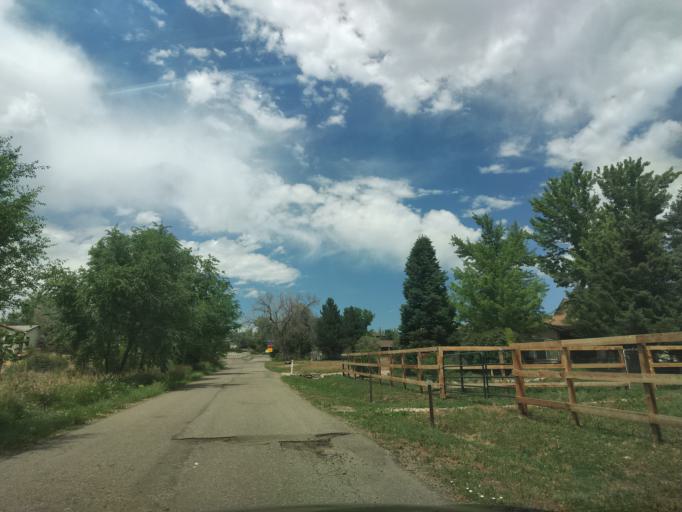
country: US
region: Colorado
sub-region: Jefferson County
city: Lakewood
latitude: 39.6722
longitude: -105.1069
